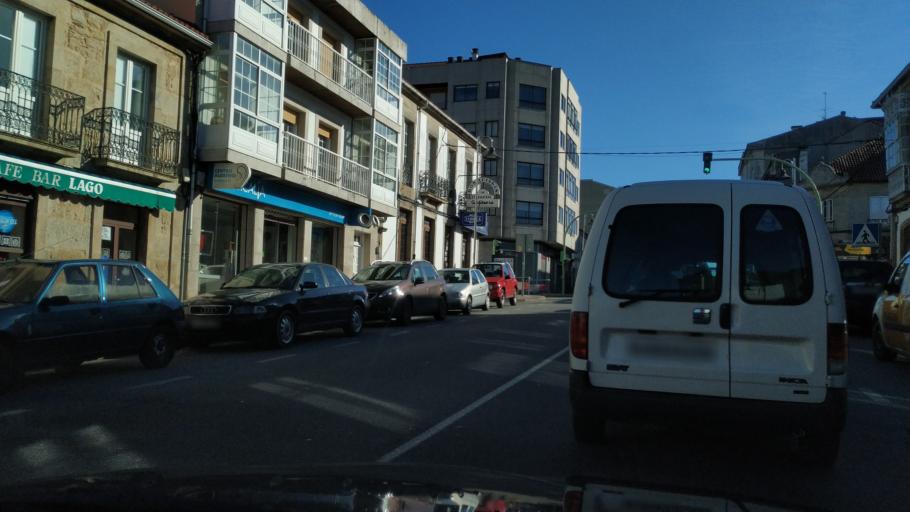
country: ES
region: Galicia
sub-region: Provincia de Pontevedra
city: Silleda
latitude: 42.6975
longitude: -8.2477
